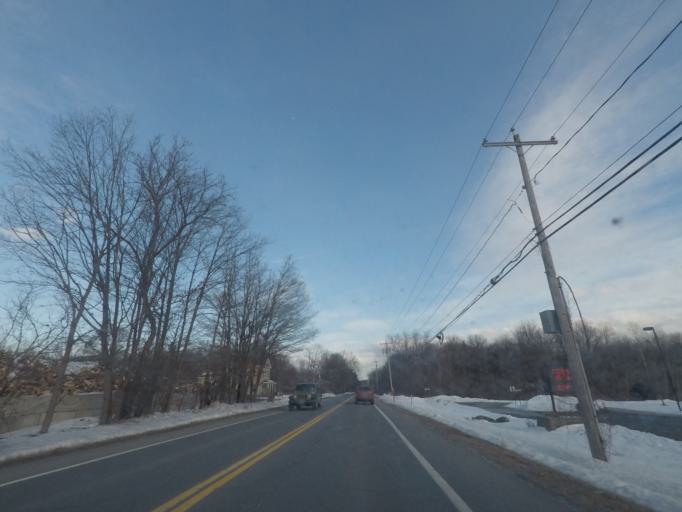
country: US
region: New York
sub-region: Schenectady County
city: Niskayuna
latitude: 42.8357
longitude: -73.8327
